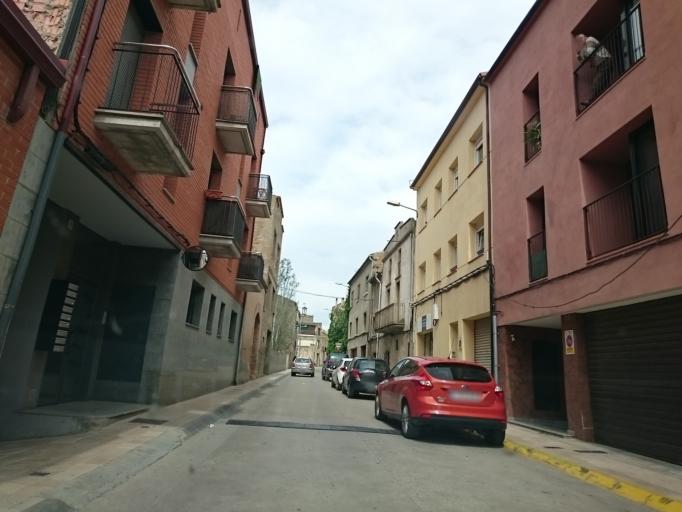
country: ES
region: Catalonia
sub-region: Provincia de Lleida
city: Mont-roig del Camp
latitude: 41.7829
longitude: 1.2858
